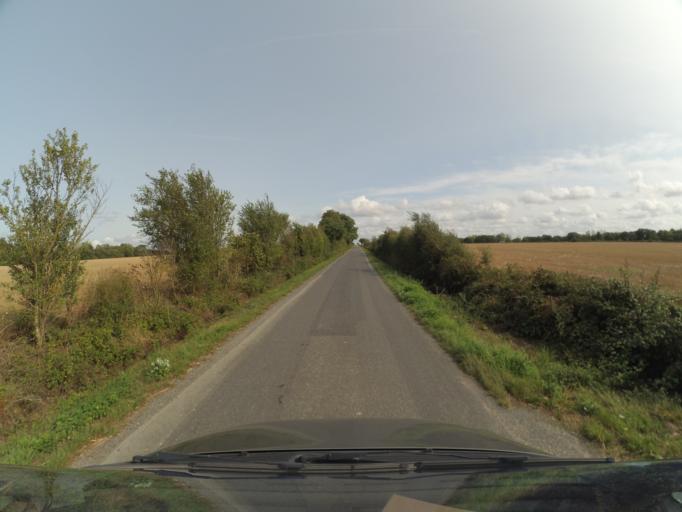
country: FR
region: Pays de la Loire
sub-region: Departement de la Vendee
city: La Bruffiere
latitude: 46.9926
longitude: -1.1902
